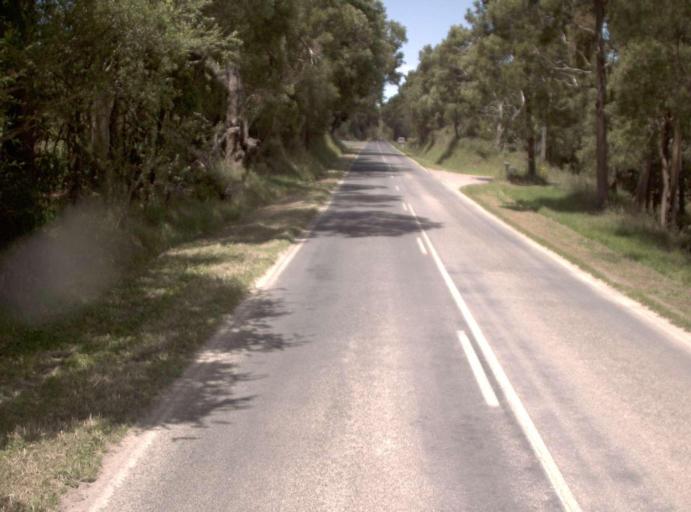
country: AU
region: Victoria
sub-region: Bass Coast
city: North Wonthaggi
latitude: -38.7246
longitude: 146.1211
